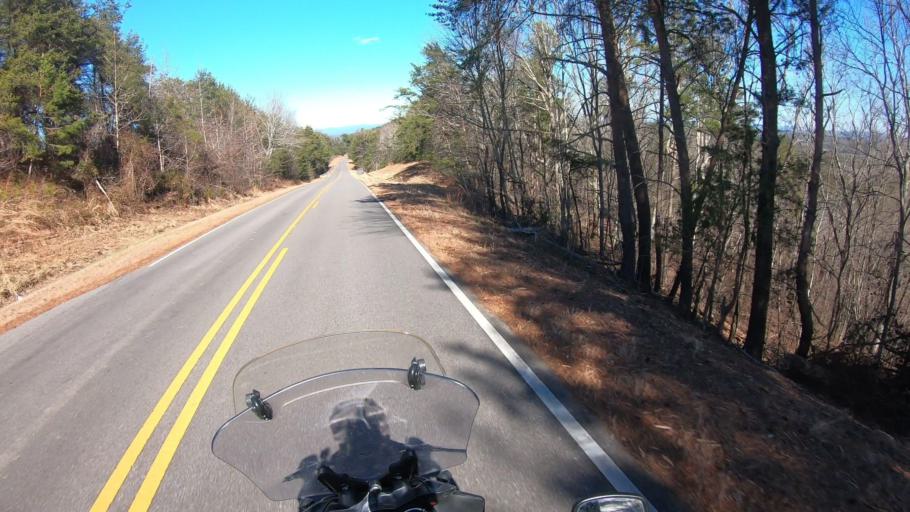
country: US
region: Alabama
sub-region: Calhoun County
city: Oxford
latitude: 33.5106
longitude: -85.7593
